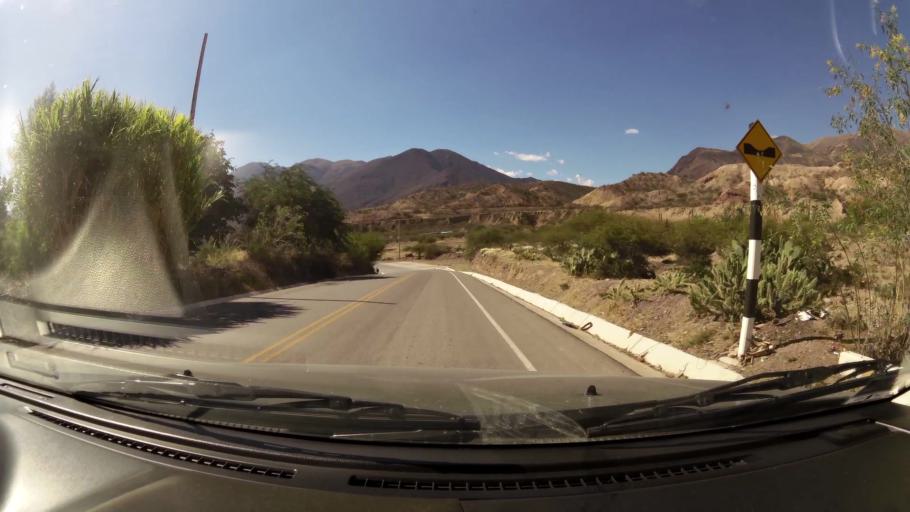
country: PE
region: Huancavelica
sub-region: Provincia de Acobamba
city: Marcas
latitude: -12.8562
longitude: -74.3293
